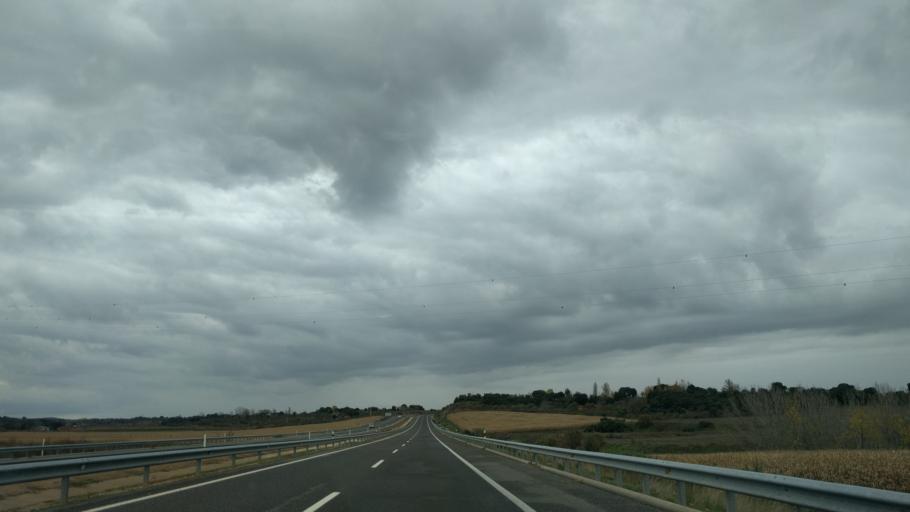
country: ES
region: Aragon
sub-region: Provincia de Huesca
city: Monzon
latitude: 41.9399
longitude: 0.1995
